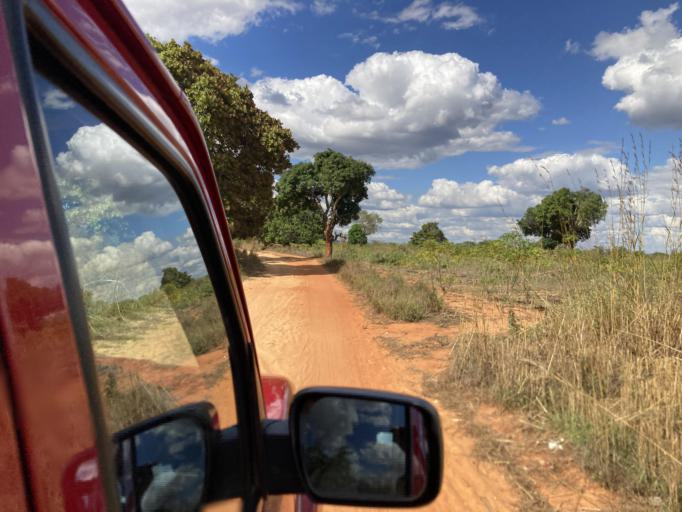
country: MZ
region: Cabo Delgado
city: Montepuez
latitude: -13.1258
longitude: 39.0450
